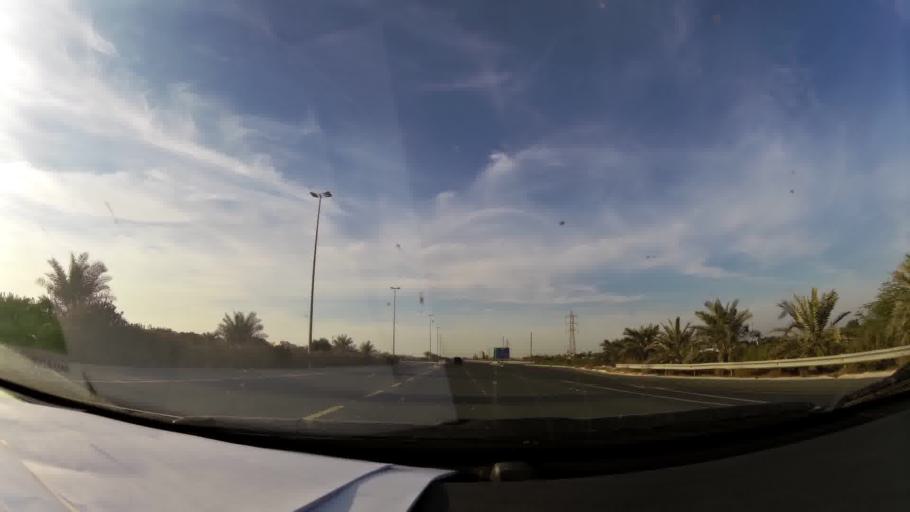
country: KW
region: Al Ahmadi
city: Al Fahahil
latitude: 28.9528
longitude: 48.1742
